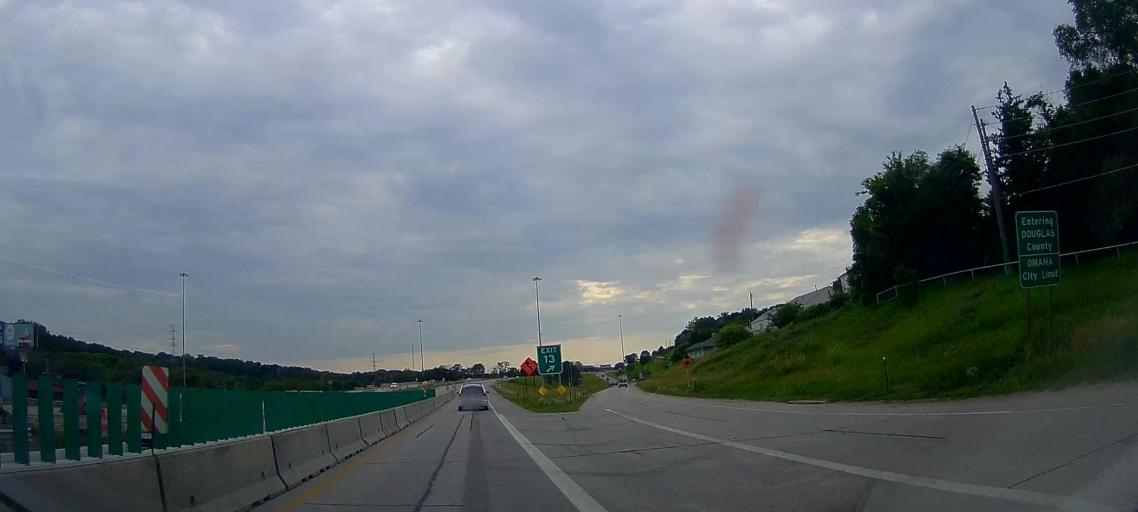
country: US
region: Iowa
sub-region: Pottawattamie County
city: Carter Lake
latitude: 41.3452
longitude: -95.9613
